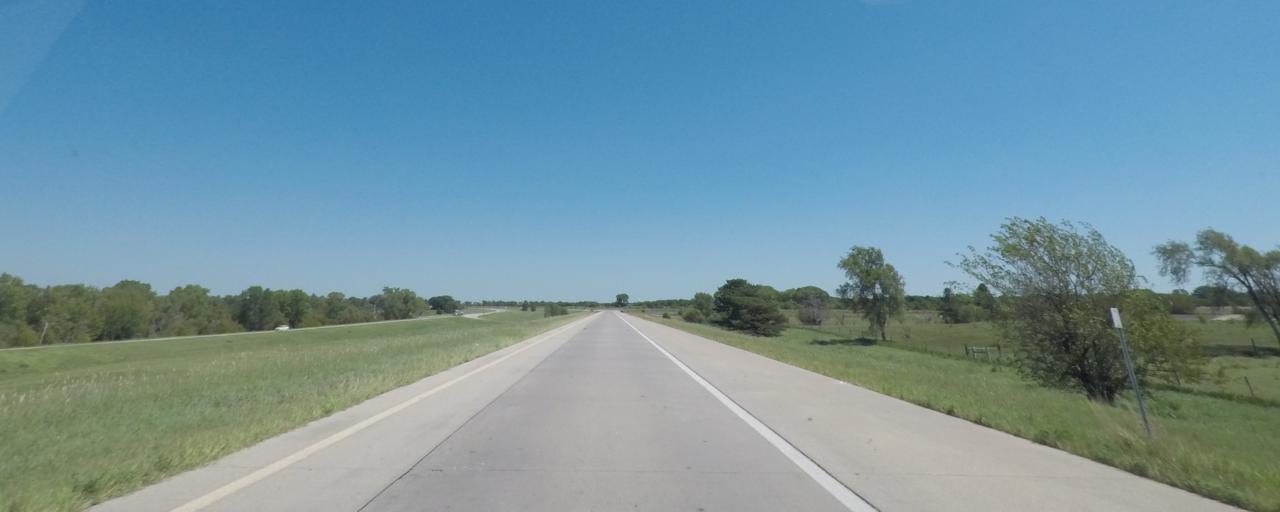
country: US
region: Kansas
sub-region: Harvey County
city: North Newton
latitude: 38.0660
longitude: -97.3167
